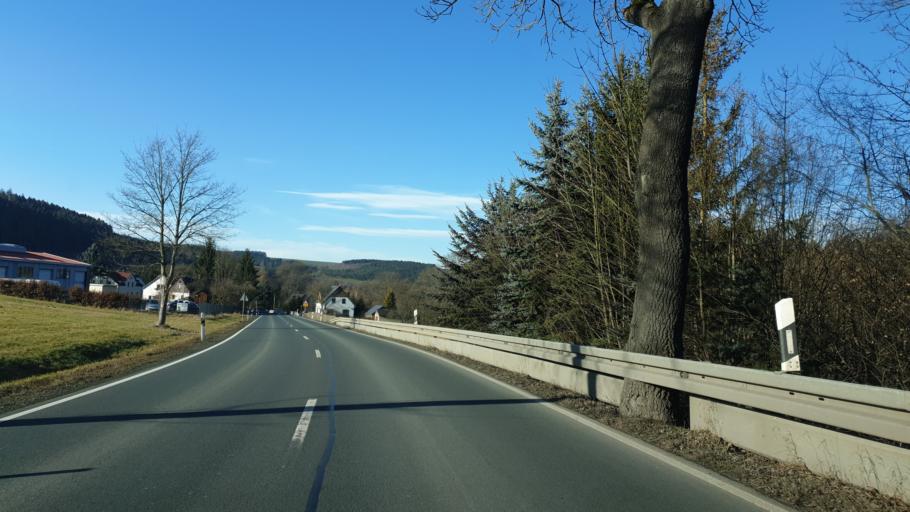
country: DE
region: Saxony
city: Adorf
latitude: 50.3496
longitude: 12.2347
